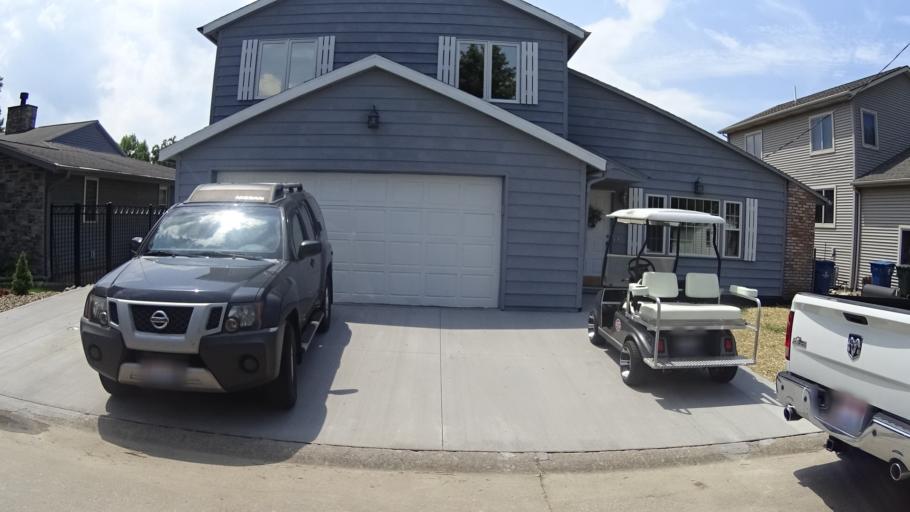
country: US
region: Ohio
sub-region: Lorain County
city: Vermilion
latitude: 41.4164
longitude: -82.3519
